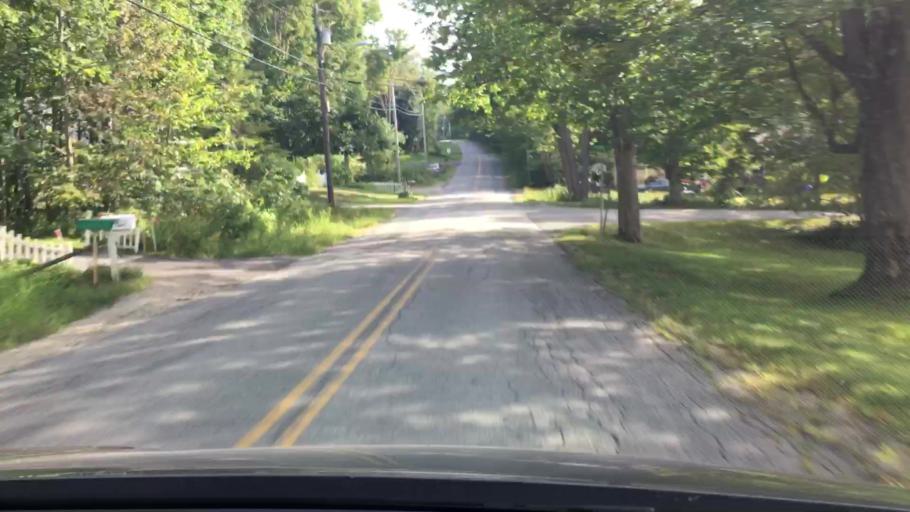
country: US
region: Maine
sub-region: Hancock County
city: Bucksport
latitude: 44.5525
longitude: -68.7961
